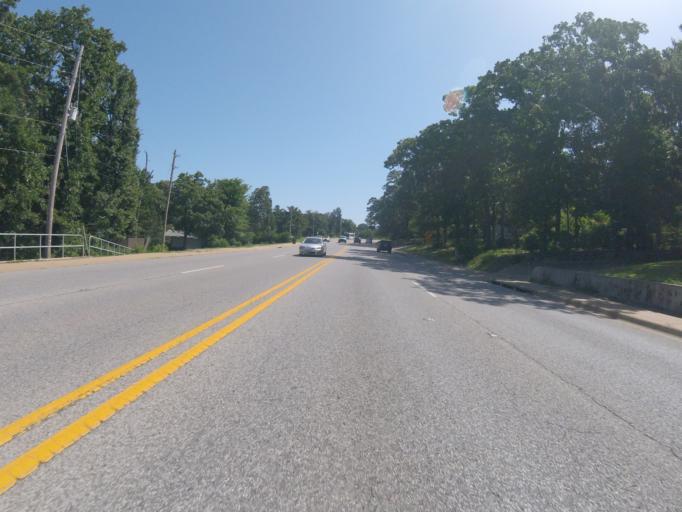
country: US
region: Arkansas
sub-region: Washington County
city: Fayetteville
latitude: 36.0785
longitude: -94.1837
